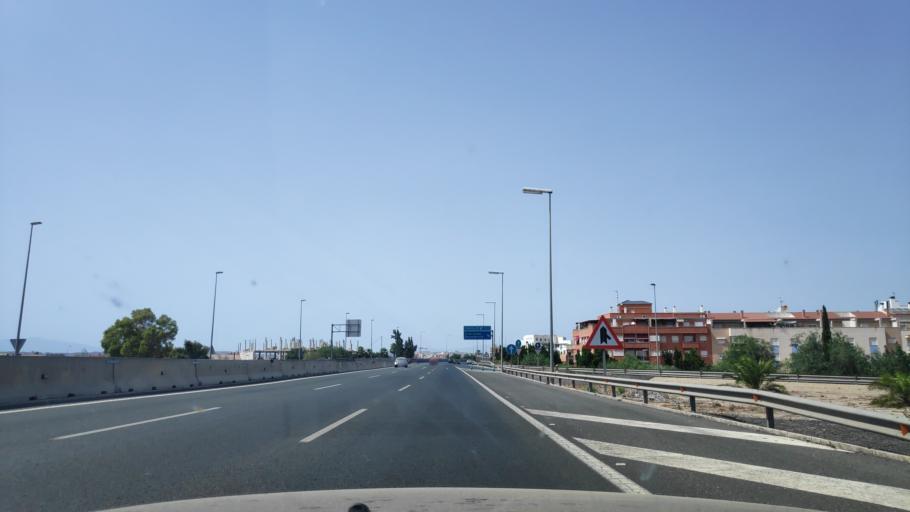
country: ES
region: Murcia
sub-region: Murcia
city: Murcia
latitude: 37.9674
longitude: -1.1372
